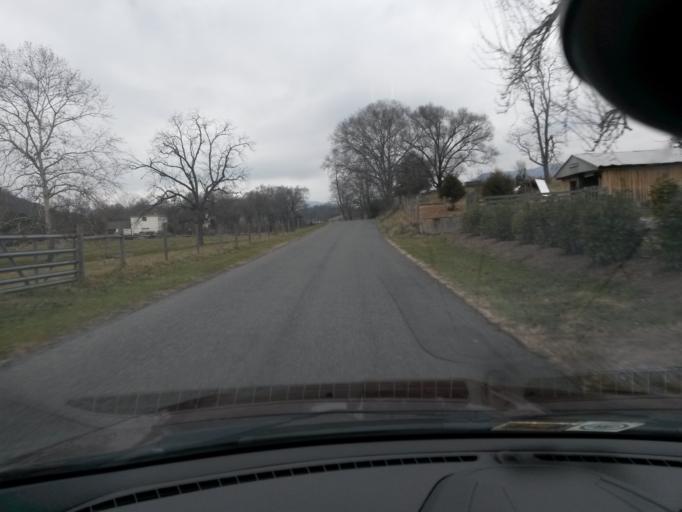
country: US
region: Virginia
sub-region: City of Lexington
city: Lexington
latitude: 37.8471
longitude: -79.4785
